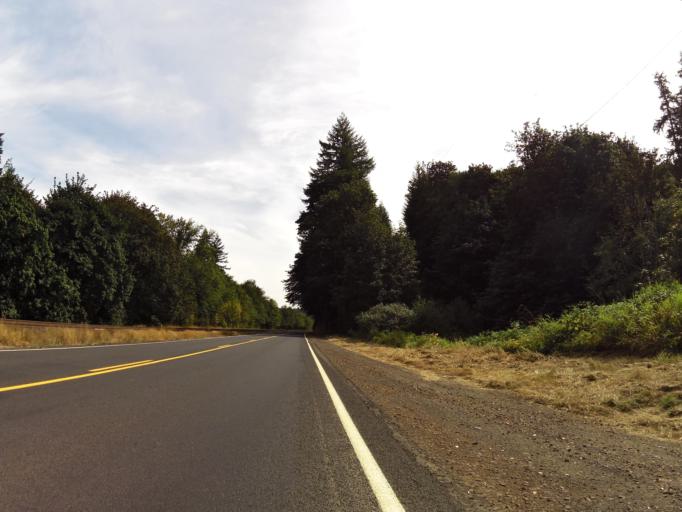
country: US
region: Washington
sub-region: Cowlitz County
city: Castle Rock
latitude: 46.3664
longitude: -122.9378
